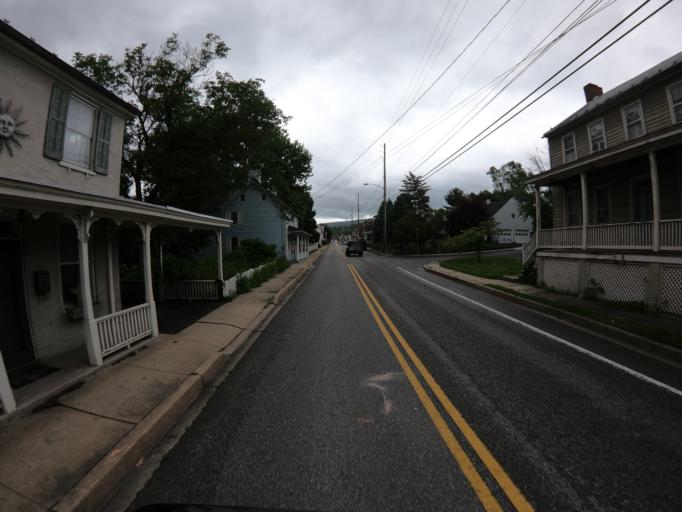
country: US
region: Maryland
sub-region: Washington County
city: Boonsboro
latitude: 39.5047
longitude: -77.6574
